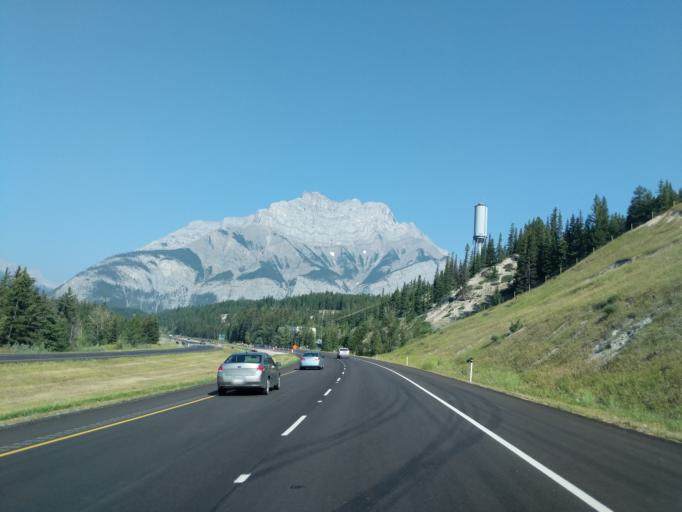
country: CA
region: Alberta
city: Banff
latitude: 51.1985
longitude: -115.4986
